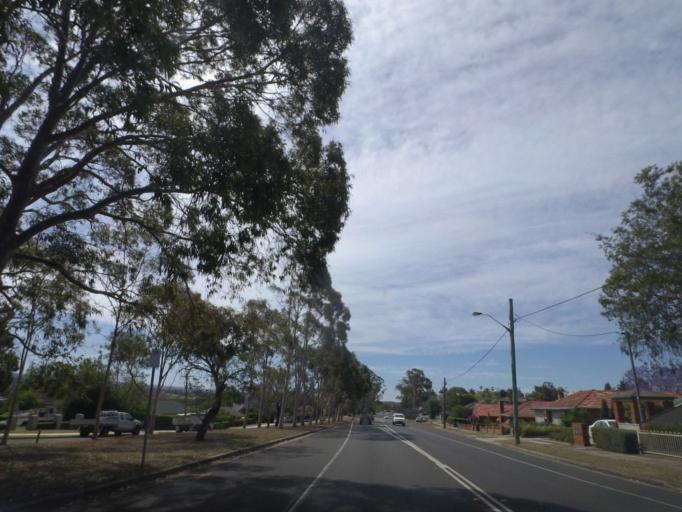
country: AU
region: New South Wales
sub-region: Camden
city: Elderslie
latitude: -34.0658
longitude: 150.6936
